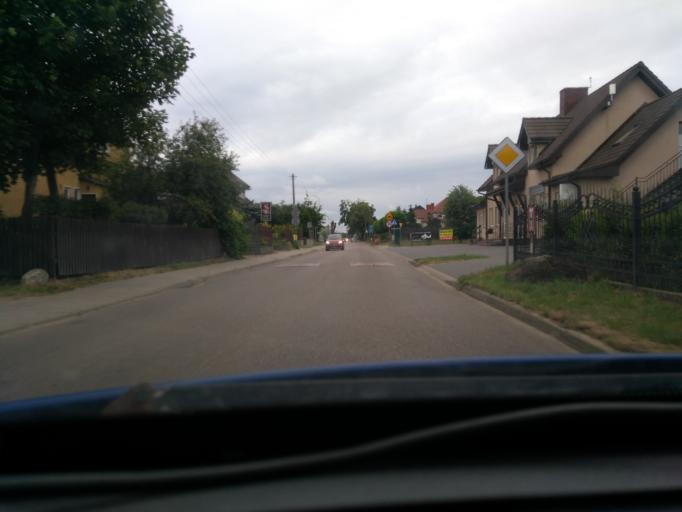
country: PL
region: Pomeranian Voivodeship
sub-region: Powiat kartuski
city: Banino
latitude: 54.3889
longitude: 18.4061
